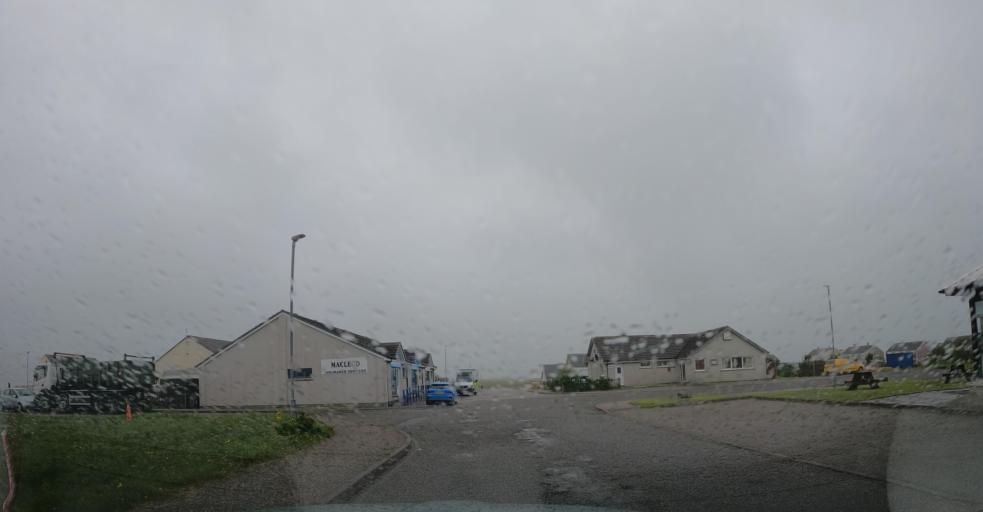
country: GB
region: Scotland
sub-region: Eilean Siar
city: Benbecula
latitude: 57.4728
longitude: -7.3784
